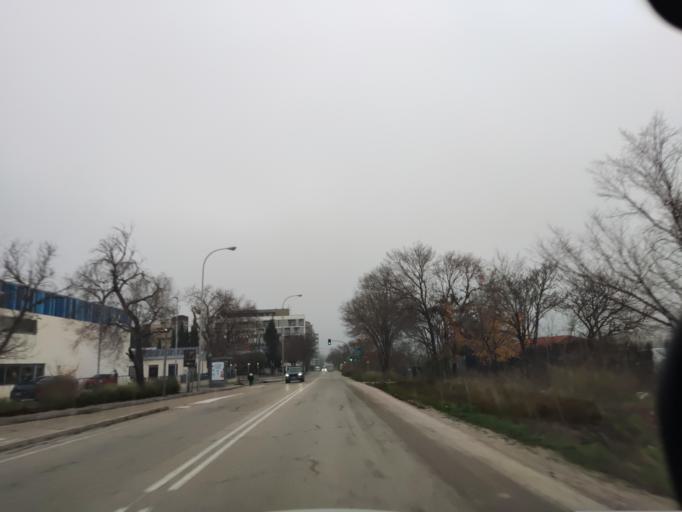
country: ES
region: Madrid
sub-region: Provincia de Madrid
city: Las Tablas
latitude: 40.5037
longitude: -3.6855
